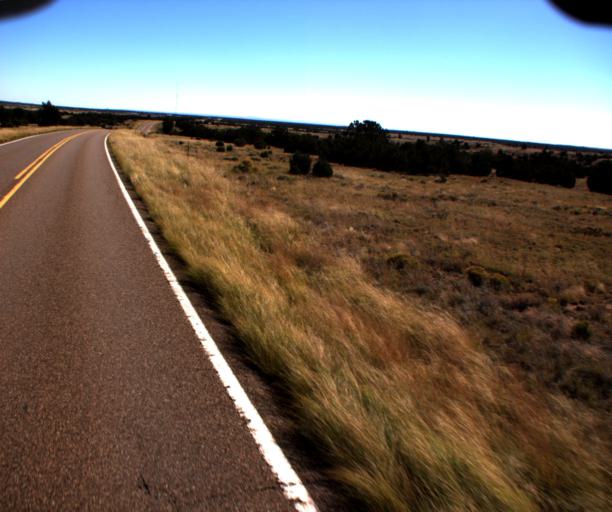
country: US
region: Arizona
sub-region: Navajo County
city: Heber-Overgaard
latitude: 34.4597
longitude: -110.4329
